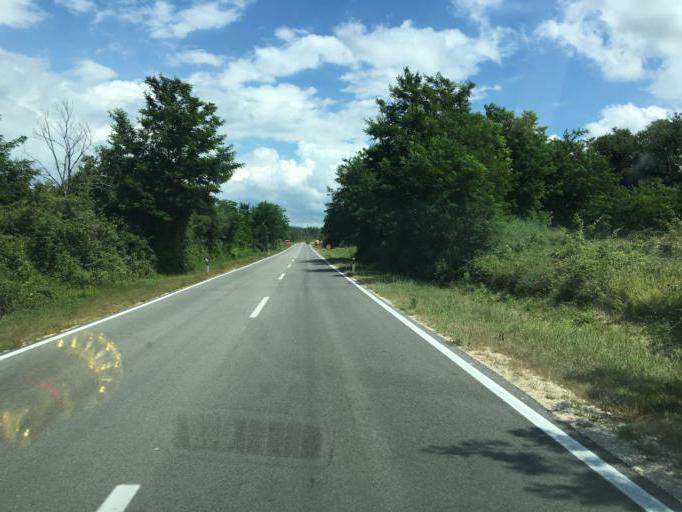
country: HR
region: Istarska
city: Karojba
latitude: 45.2121
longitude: 13.7643
